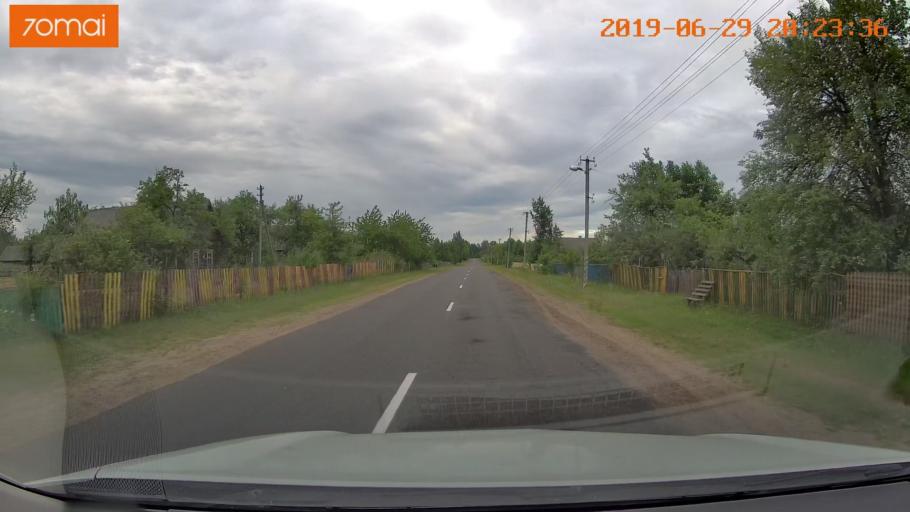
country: BY
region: Brest
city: Asnyezhytsy
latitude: 52.4465
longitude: 26.2615
